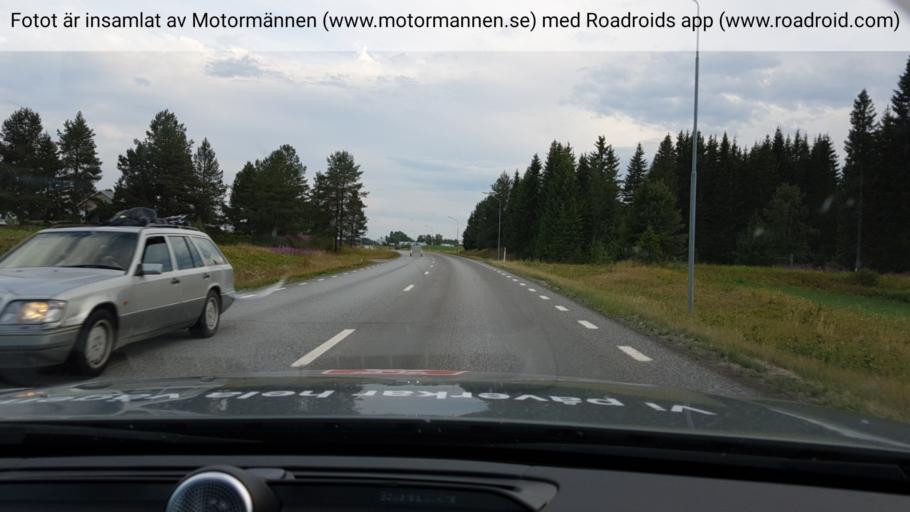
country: SE
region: Jaemtland
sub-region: Stroemsunds Kommun
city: Stroemsund
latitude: 63.5038
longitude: 15.2655
